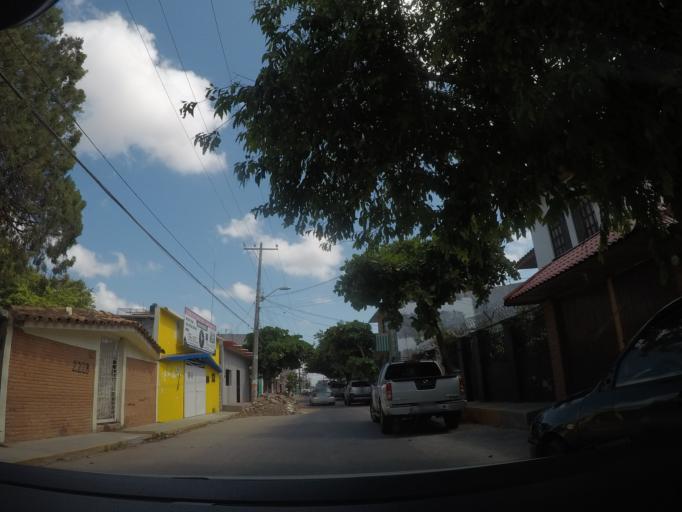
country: MX
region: Oaxaca
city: Juchitan de Zaragoza
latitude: 16.4394
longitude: -95.0208
